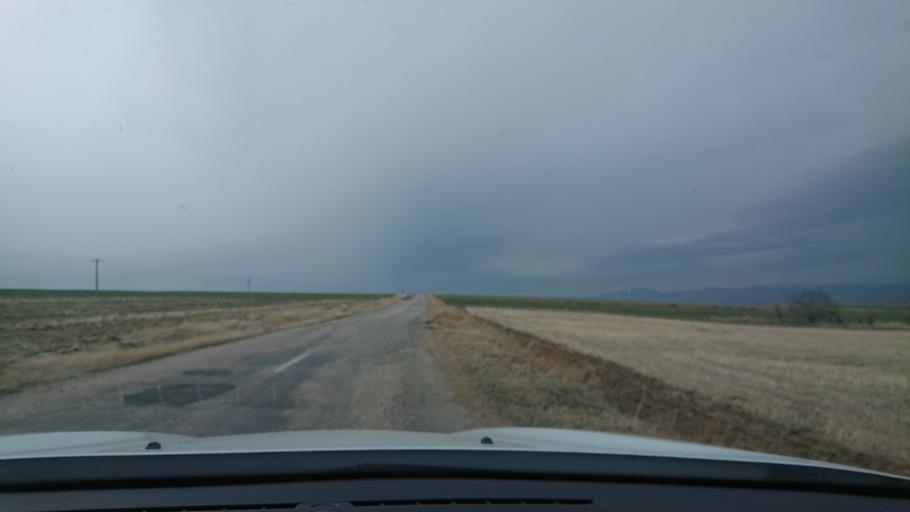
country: TR
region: Aksaray
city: Agacoren
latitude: 38.9443
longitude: 33.9096
